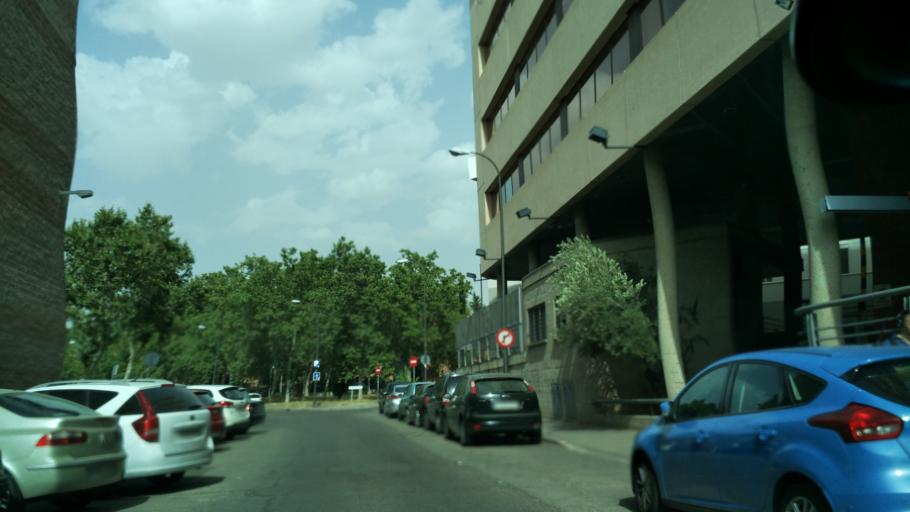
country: ES
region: Madrid
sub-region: Provincia de Madrid
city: Pinar de Chamartin
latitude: 40.4884
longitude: -3.6899
